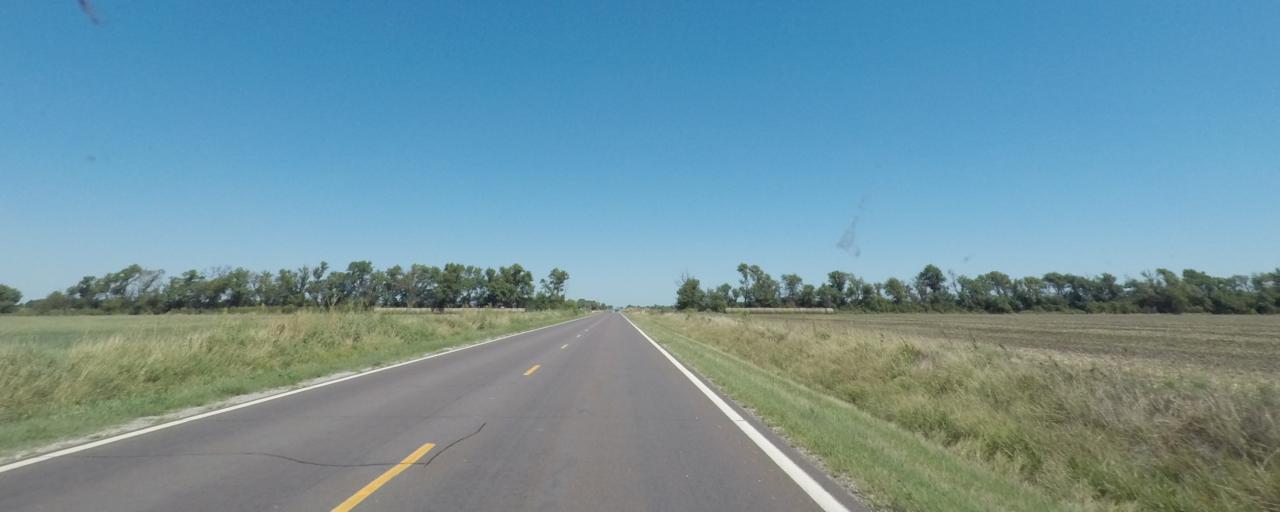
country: US
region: Kansas
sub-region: Sumner County
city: Wellington
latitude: 37.1497
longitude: -97.4023
